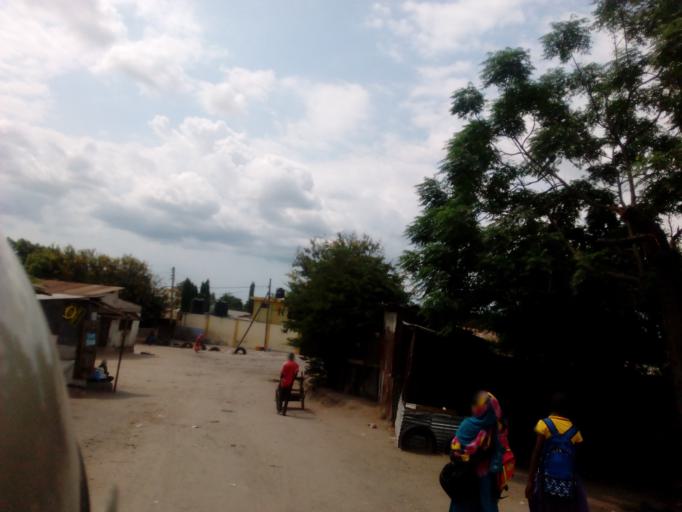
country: TZ
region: Dar es Salaam
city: Dar es Salaam
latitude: -6.8548
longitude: 39.2544
